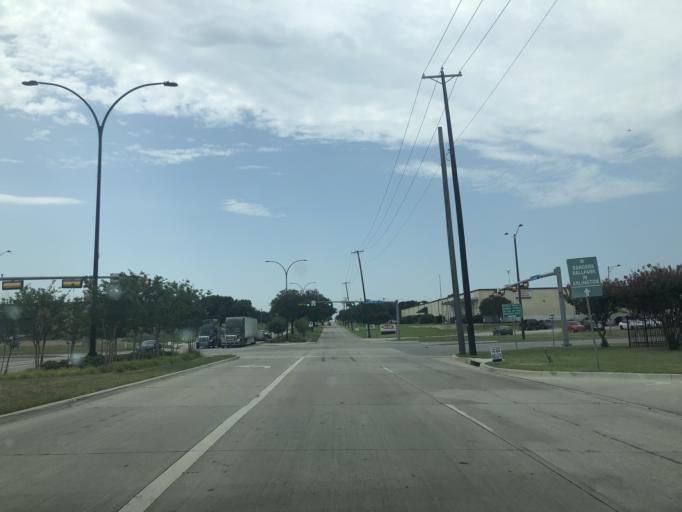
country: US
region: Texas
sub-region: Dallas County
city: Grand Prairie
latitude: 32.7494
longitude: -97.0459
